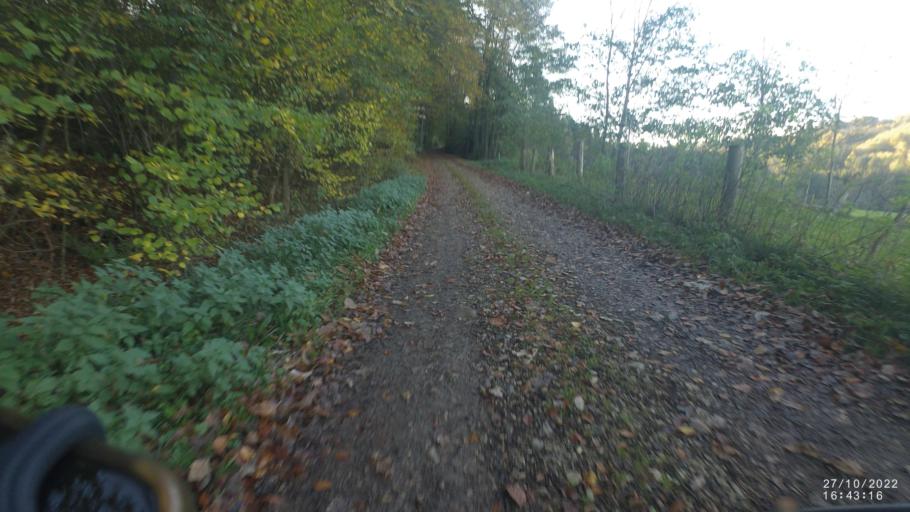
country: DE
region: Baden-Wuerttemberg
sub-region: Regierungsbezirk Stuttgart
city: Gingen an der Fils
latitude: 48.6487
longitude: 9.7668
